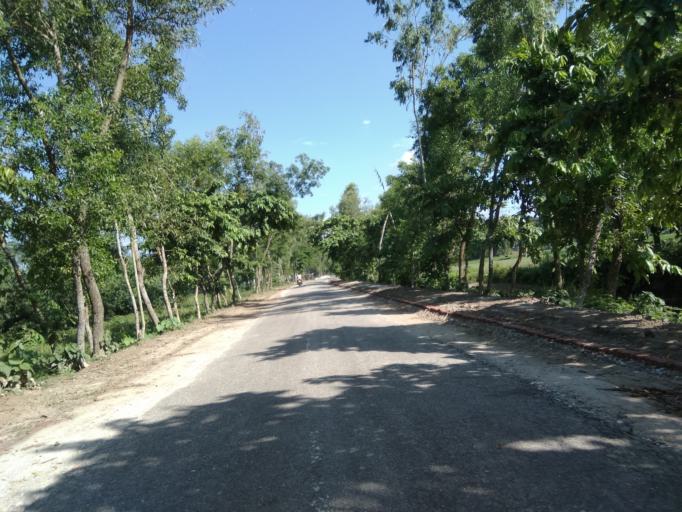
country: BD
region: Rangpur Division
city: Panchagarh
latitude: 26.2529
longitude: 88.6247
